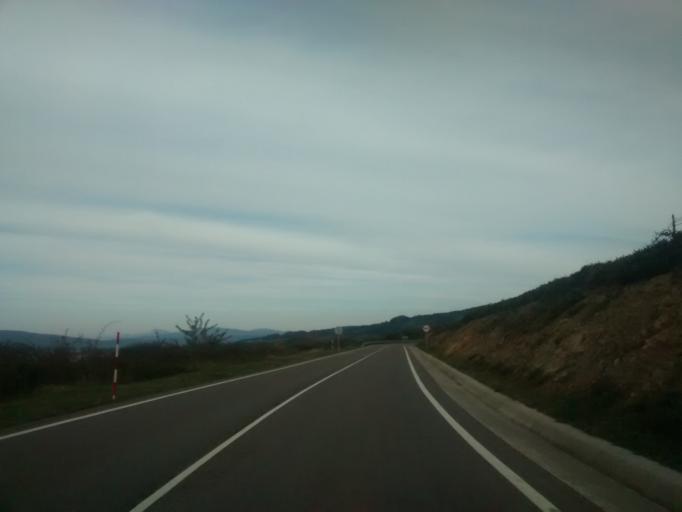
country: ES
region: Castille and Leon
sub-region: Provincia de Burgos
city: Arija
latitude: 42.9730
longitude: -4.0138
